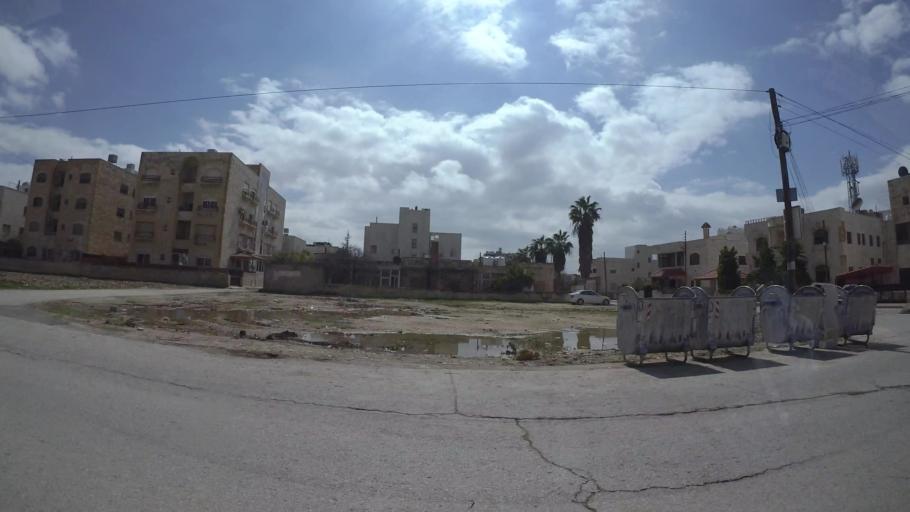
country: JO
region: Amman
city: Wadi as Sir
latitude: 31.9657
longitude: 35.8371
